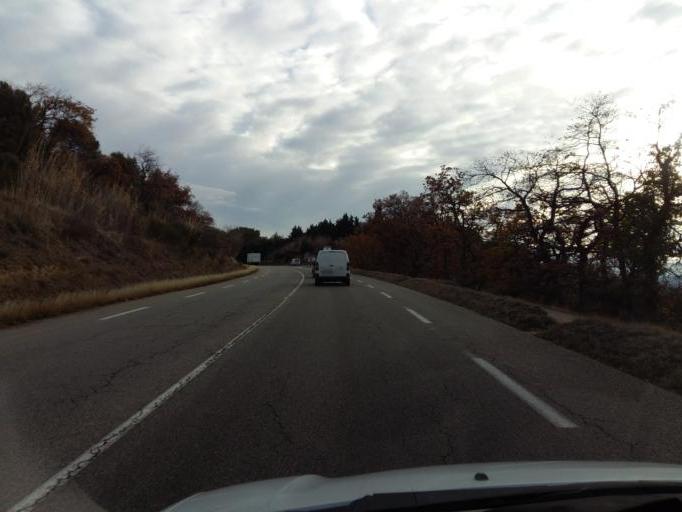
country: FR
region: Provence-Alpes-Cote d'Azur
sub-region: Departement du Vaucluse
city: Visan
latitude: 44.3278
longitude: 4.9458
